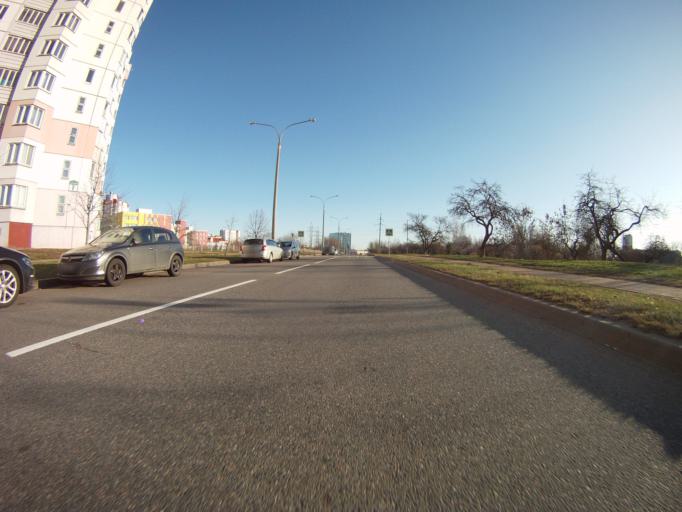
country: BY
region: Minsk
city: Novoye Medvezhino
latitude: 53.8767
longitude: 27.4856
